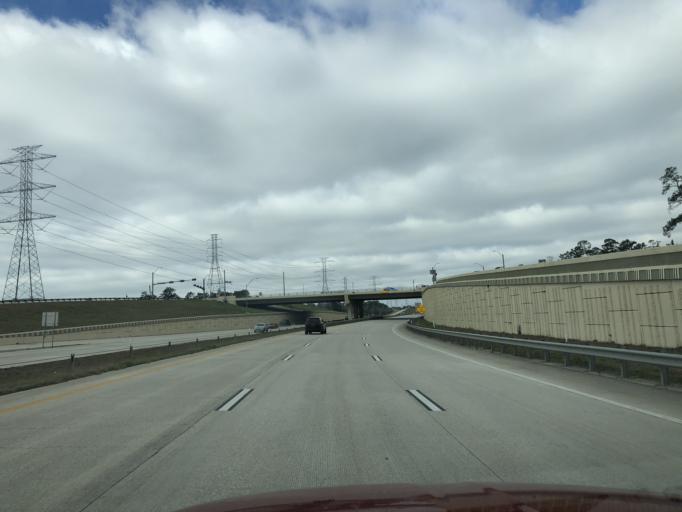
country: US
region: Texas
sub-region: Harris County
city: Spring
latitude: 30.0879
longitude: -95.4485
